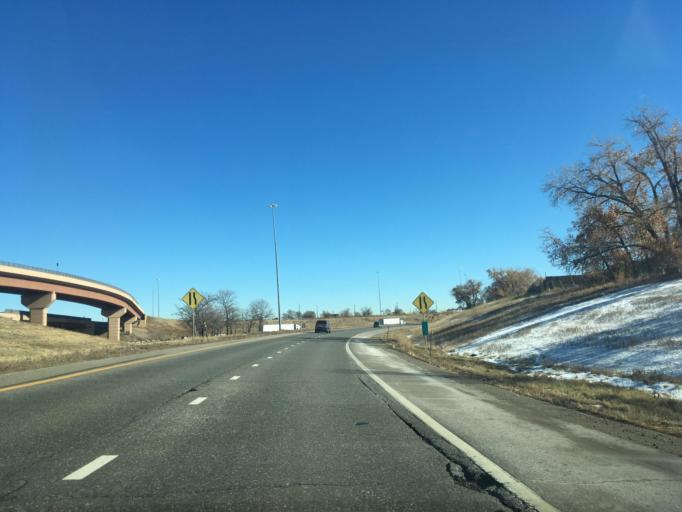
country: US
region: Colorado
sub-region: Adams County
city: Welby
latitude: 39.8229
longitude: -104.9662
